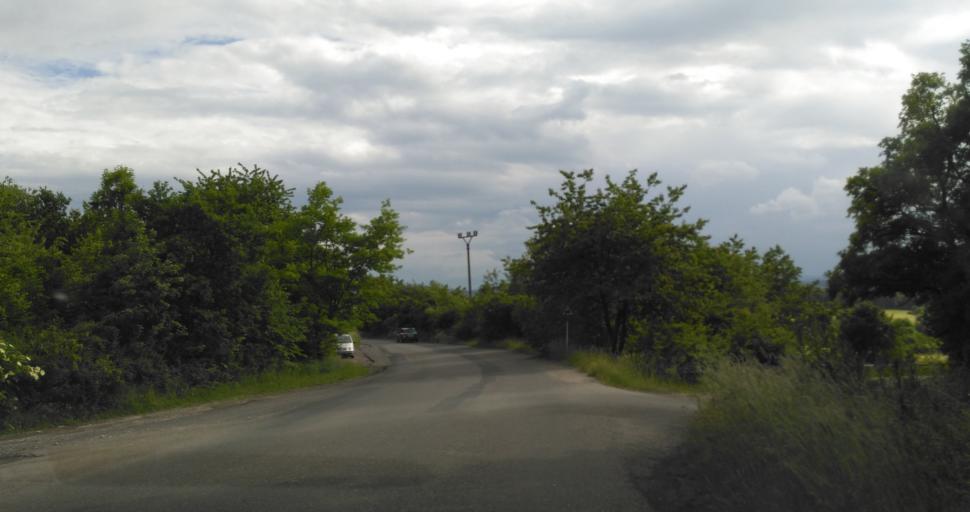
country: CZ
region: Central Bohemia
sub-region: Okres Beroun
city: Beroun
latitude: 49.9006
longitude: 14.0772
